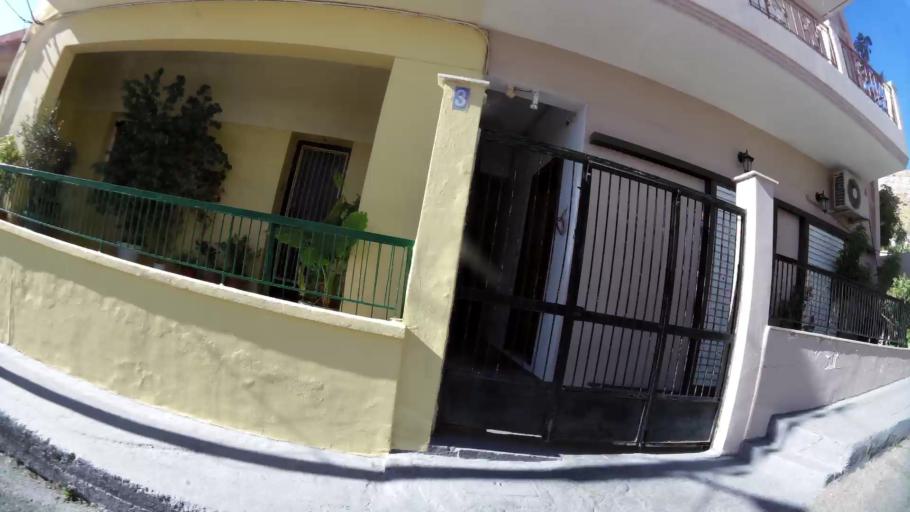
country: GR
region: Attica
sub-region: Nomos Piraios
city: Keratsini
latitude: 37.9647
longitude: 23.6063
